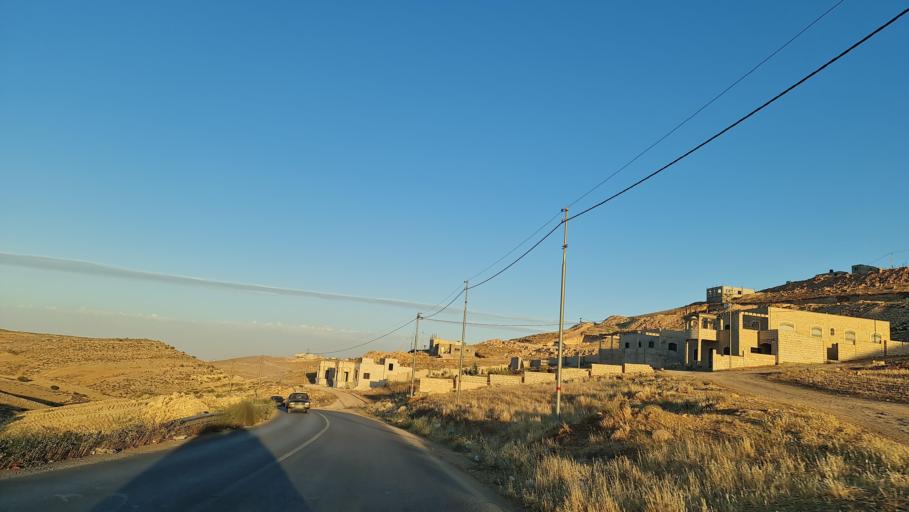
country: JO
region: Zarqa
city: Zarqa
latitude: 32.0841
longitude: 36.0299
